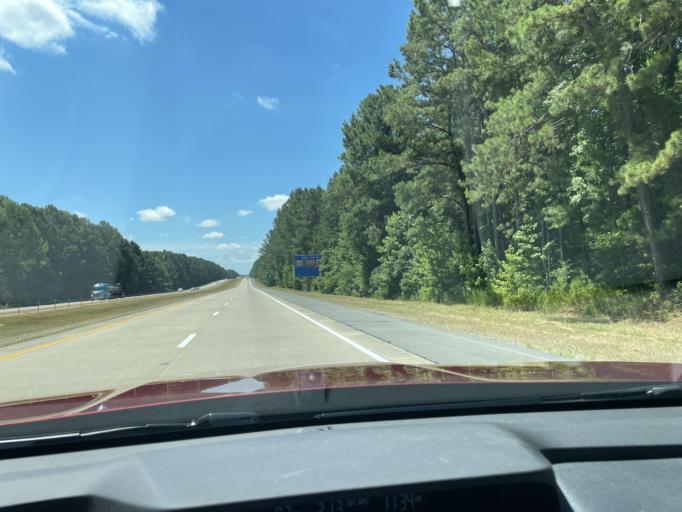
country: US
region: Arkansas
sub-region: Jefferson County
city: Redfield
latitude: 34.4600
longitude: -92.2039
